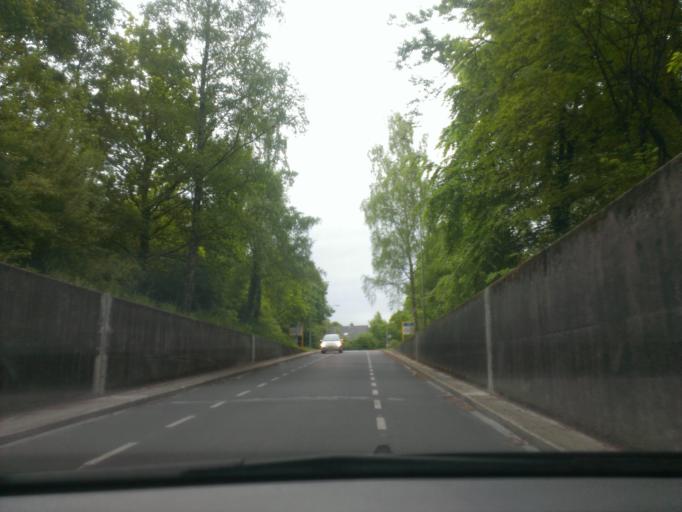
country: NL
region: Gelderland
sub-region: Gemeente Epe
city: Epe
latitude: 52.3432
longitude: 5.9695
